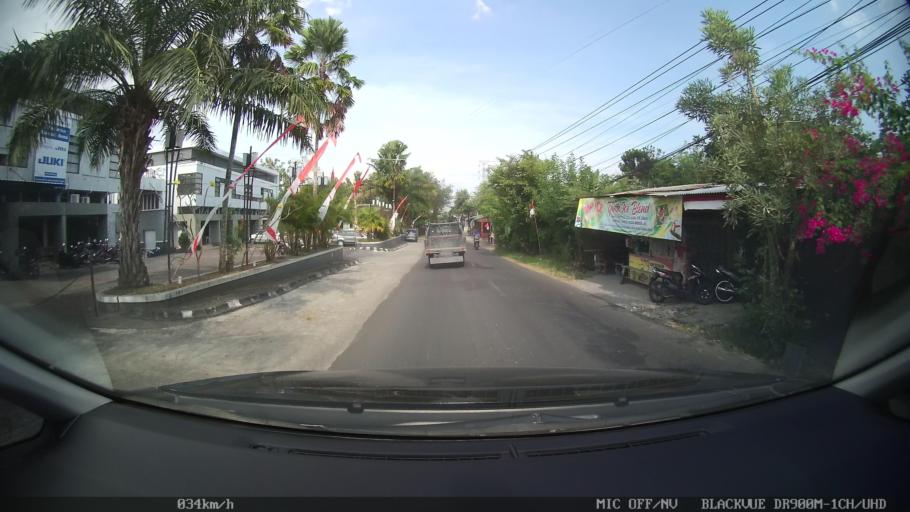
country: ID
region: Daerah Istimewa Yogyakarta
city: Kasihan
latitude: -7.8390
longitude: 110.3213
